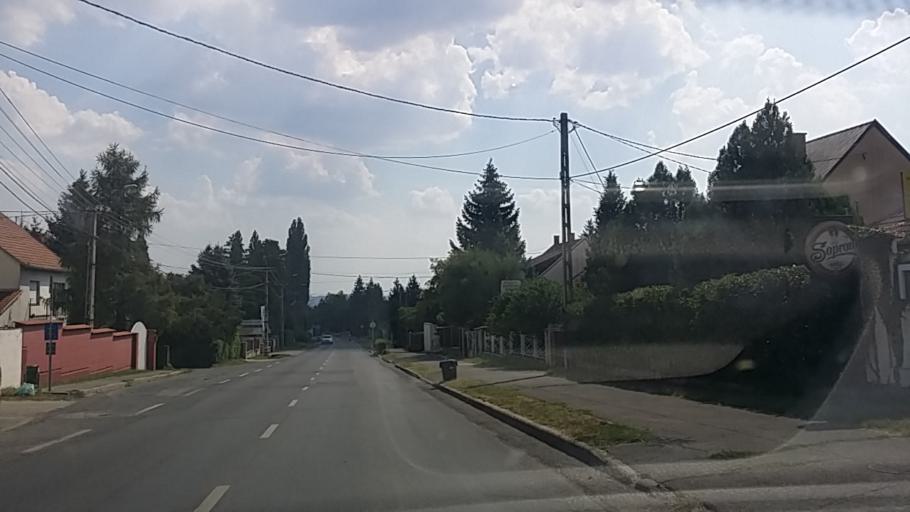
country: HU
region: Baranya
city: Pecs
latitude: 46.0766
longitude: 18.1870
